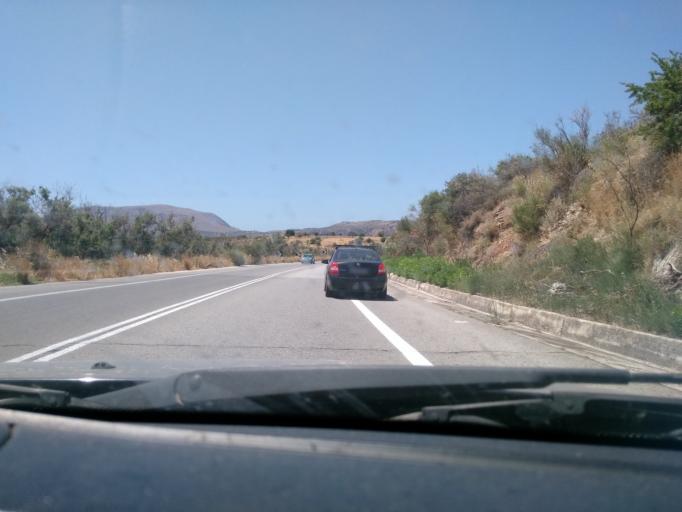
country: GR
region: Crete
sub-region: Nomos Chanias
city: Kalivai
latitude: 35.4298
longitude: 24.1674
